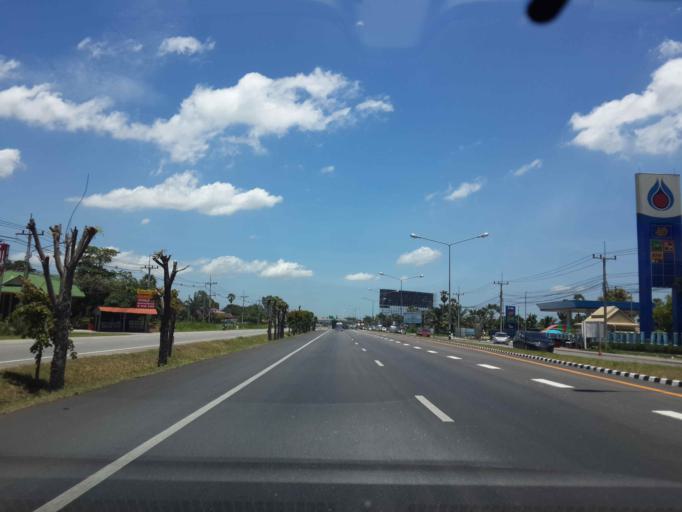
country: TH
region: Phetchaburi
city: Ban Lat
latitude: 13.0508
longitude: 99.9404
